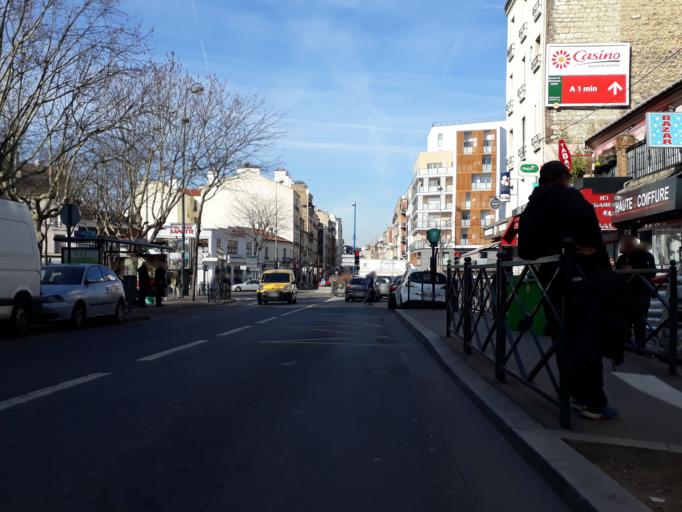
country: FR
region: Ile-de-France
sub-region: Departement des Hauts-de-Seine
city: Asnieres-sur-Seine
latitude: 48.9121
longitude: 2.2966
